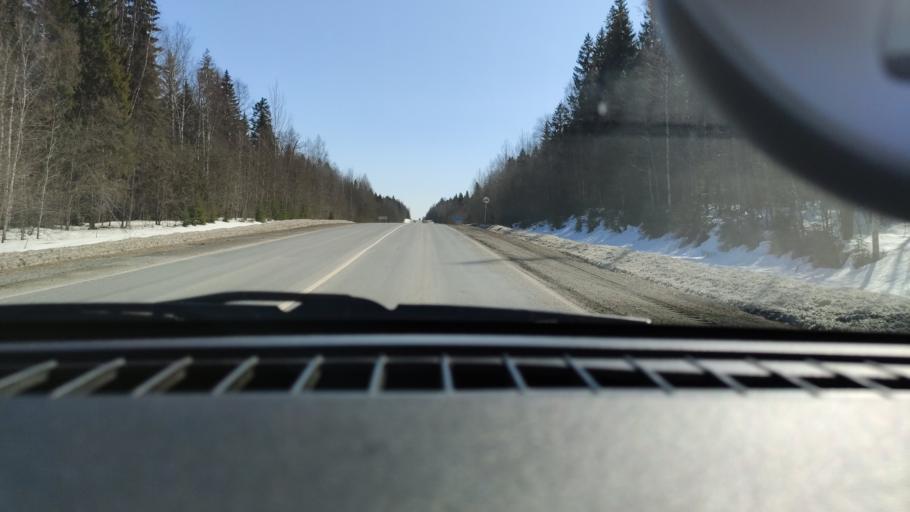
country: RU
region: Perm
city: Perm
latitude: 58.1607
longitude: 56.2456
